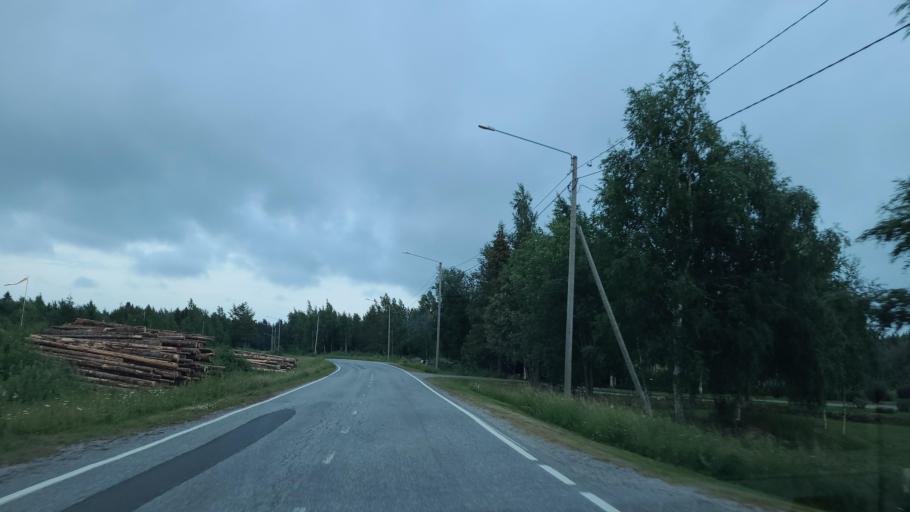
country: FI
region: Ostrobothnia
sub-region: Vaasa
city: Replot
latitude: 63.2820
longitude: 21.1272
